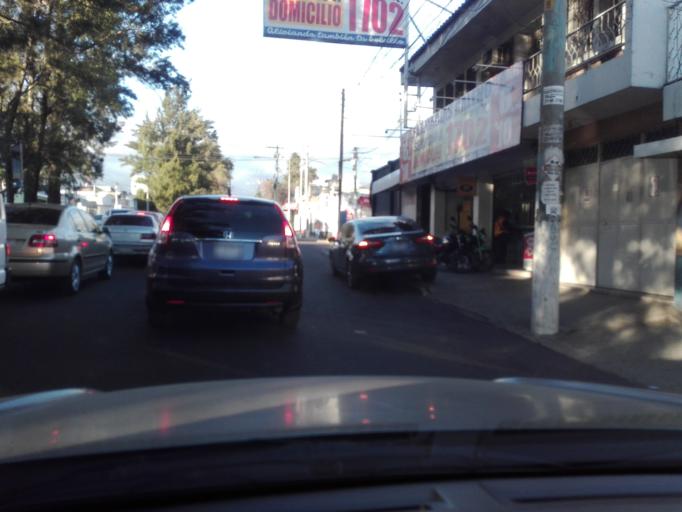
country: GT
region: Guatemala
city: Mixco
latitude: 14.5882
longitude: -90.5795
